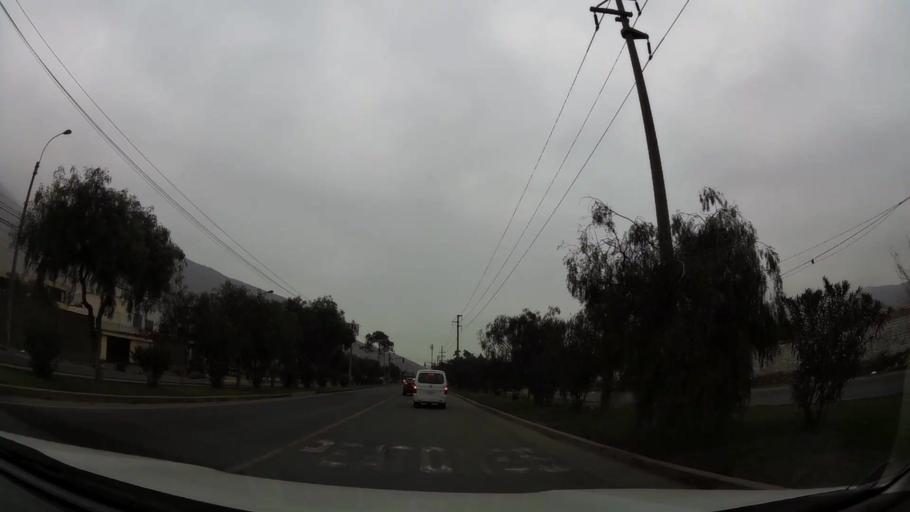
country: PE
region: Lima
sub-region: Lima
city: La Molina
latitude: -12.0860
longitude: -76.8993
